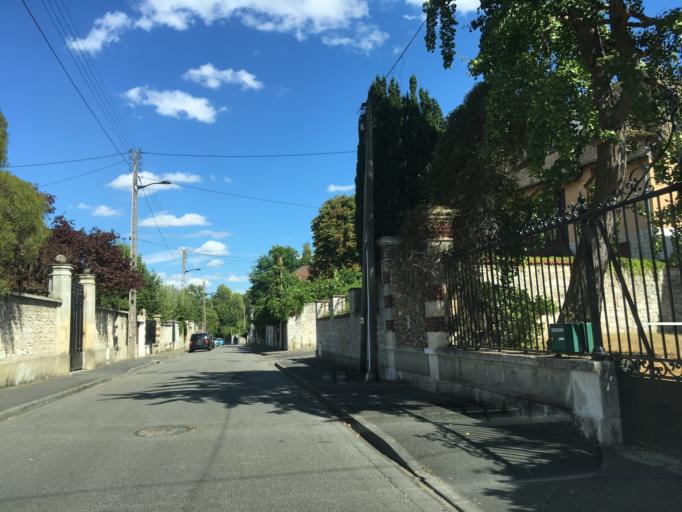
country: FR
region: Haute-Normandie
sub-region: Departement de l'Eure
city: Vernon
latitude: 49.0886
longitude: 1.4742
